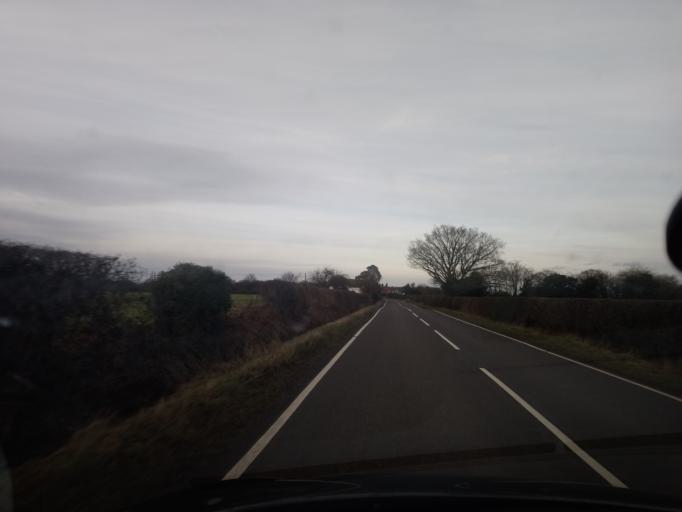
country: GB
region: England
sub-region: Shropshire
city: Prees
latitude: 52.9170
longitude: -2.6826
